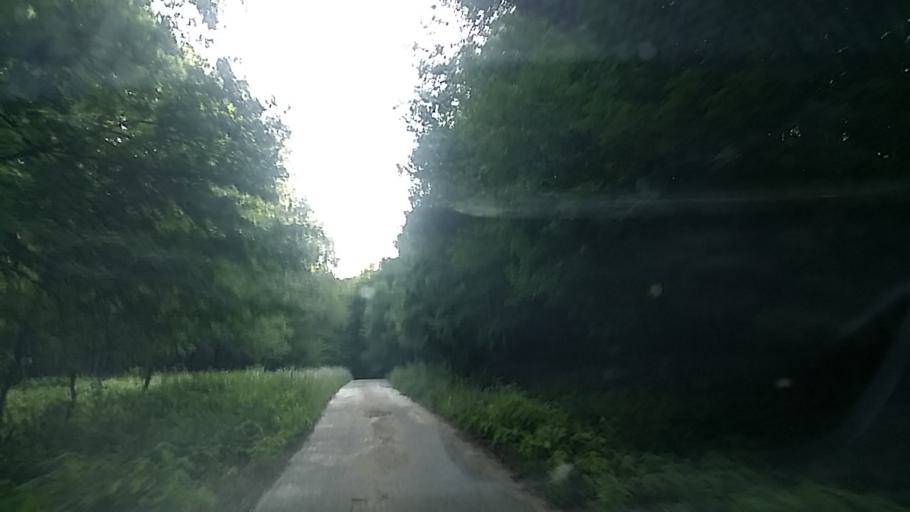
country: HU
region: Komarom-Esztergom
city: Tatabanya
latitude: 47.5956
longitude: 18.4280
